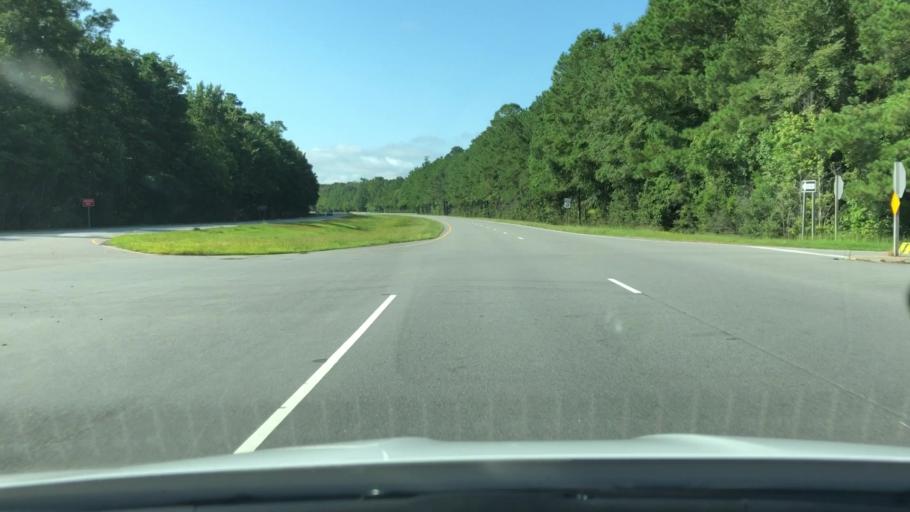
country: US
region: North Carolina
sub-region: Pasquotank County
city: Elizabeth City
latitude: 36.4268
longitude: -76.3424
